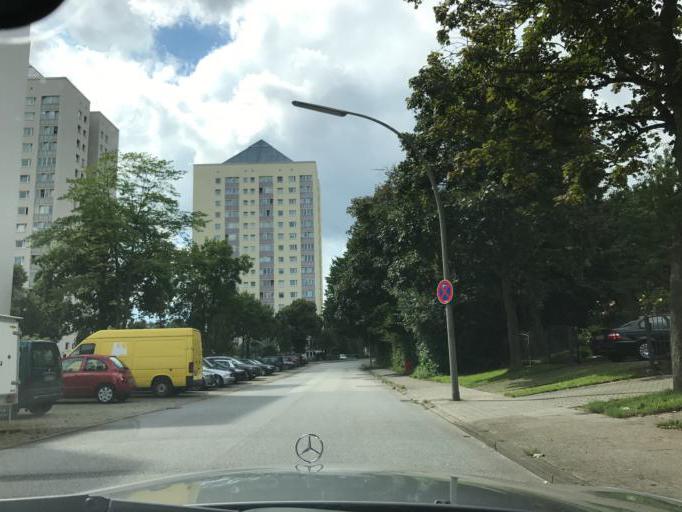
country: DE
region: Hamburg
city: Bergedorf
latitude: 53.5101
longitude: 10.2096
